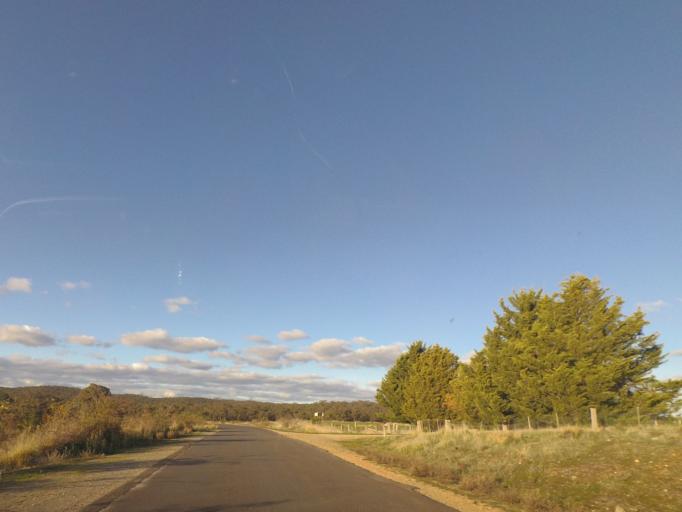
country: AU
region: Victoria
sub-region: Mount Alexander
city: Castlemaine
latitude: -37.1591
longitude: 144.2180
